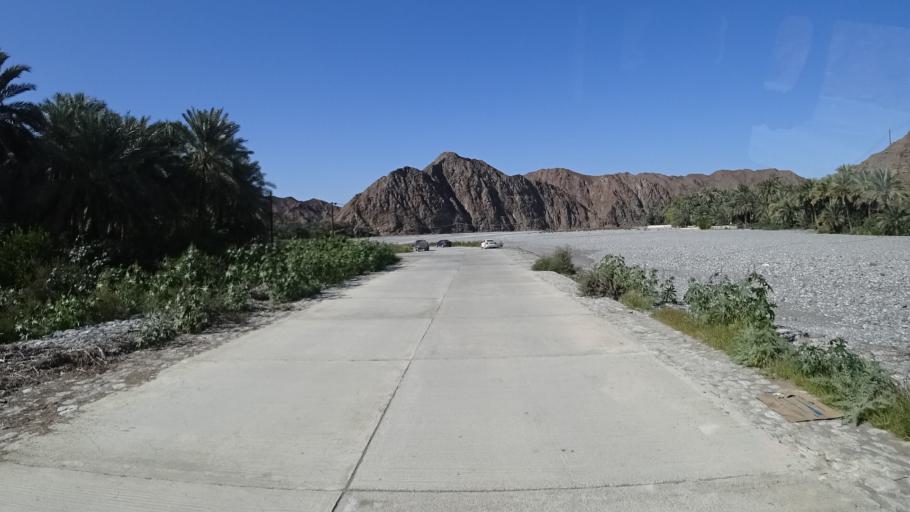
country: OM
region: Al Batinah
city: Bayt al `Awabi
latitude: 23.3844
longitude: 57.6614
